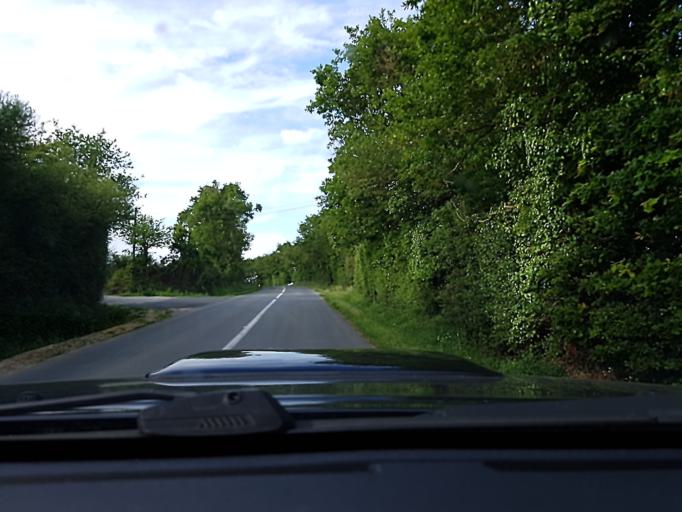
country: FR
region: Pays de la Loire
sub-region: Departement de la Vendee
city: Mache
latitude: 46.7743
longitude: -1.6679
